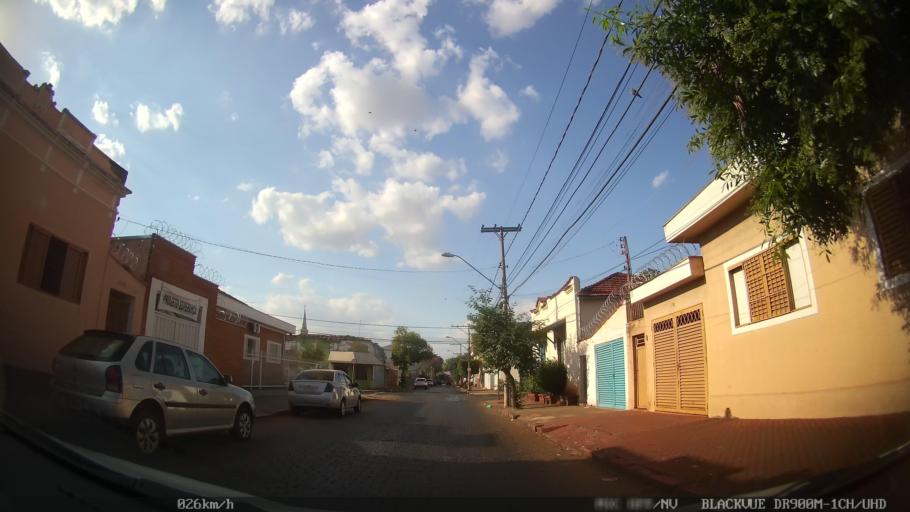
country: BR
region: Sao Paulo
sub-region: Ribeirao Preto
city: Ribeirao Preto
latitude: -21.1714
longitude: -47.8185
